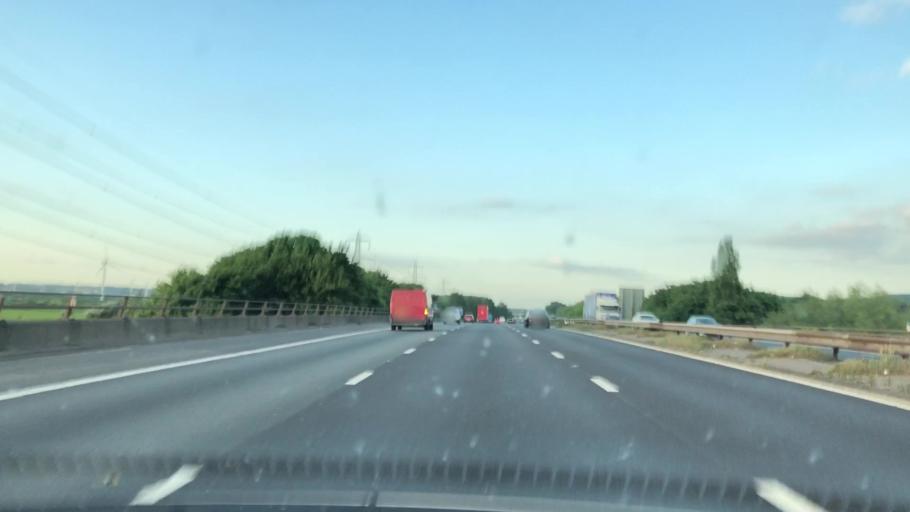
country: GB
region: England
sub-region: Cheshire West and Chester
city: Helsby
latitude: 53.2742
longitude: -2.7838
